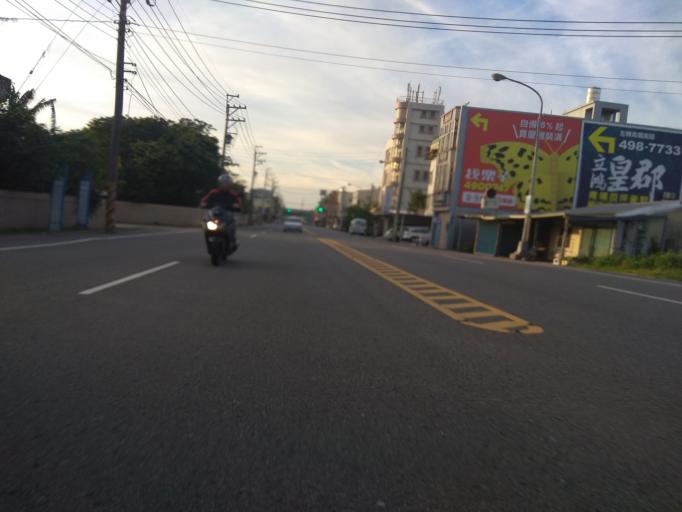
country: TW
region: Taiwan
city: Taoyuan City
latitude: 24.9829
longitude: 121.1900
